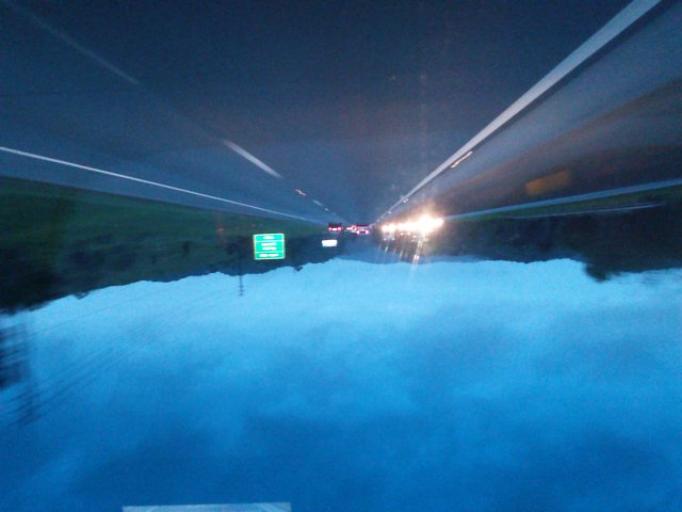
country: BR
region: Santa Catarina
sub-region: Penha
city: Penha
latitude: -26.7874
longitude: -48.6820
